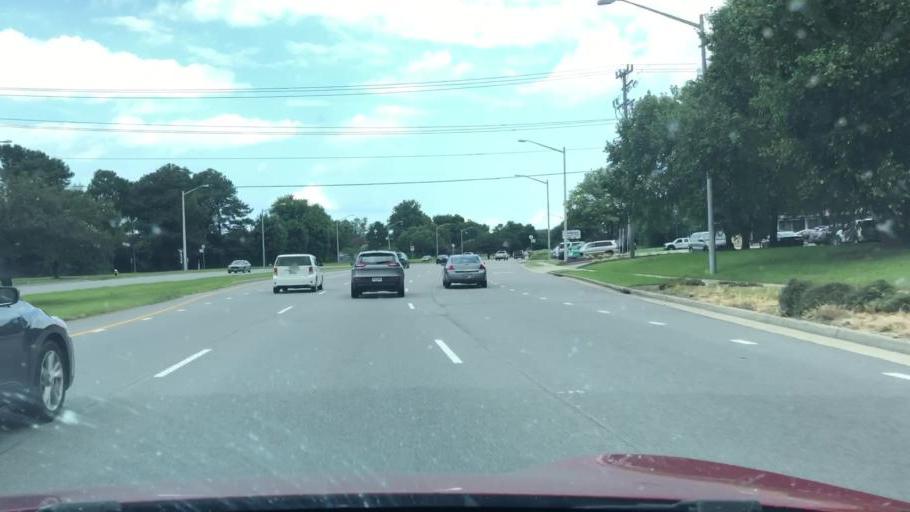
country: US
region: Virginia
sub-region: City of Chesapeake
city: Chesapeake
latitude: 36.8510
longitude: -76.1364
